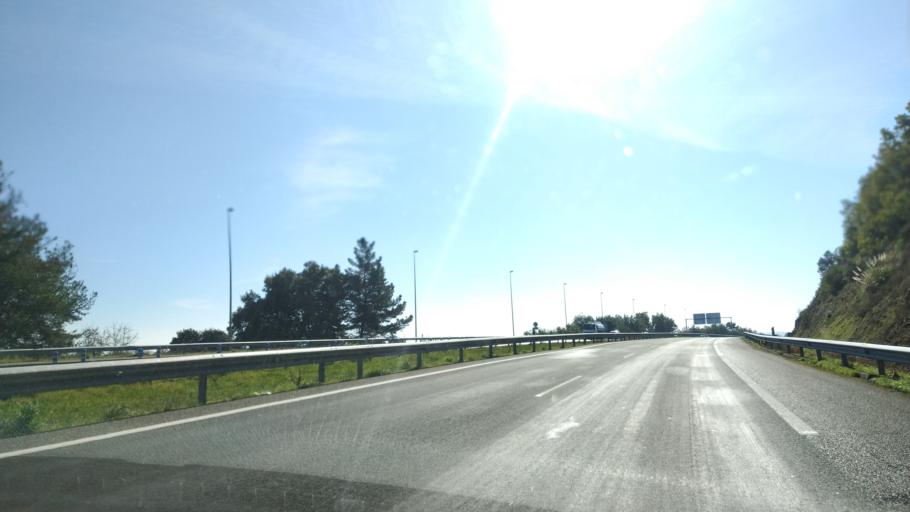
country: ES
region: Galicia
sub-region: Provincia de Ourense
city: Ourense
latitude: 42.3414
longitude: -7.8853
